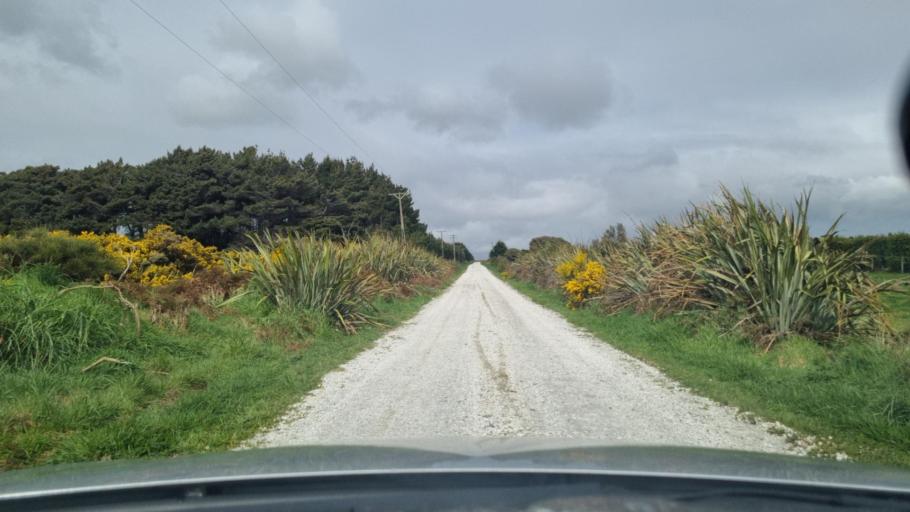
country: NZ
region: Southland
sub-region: Invercargill City
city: Bluff
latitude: -46.5117
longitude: 168.3523
